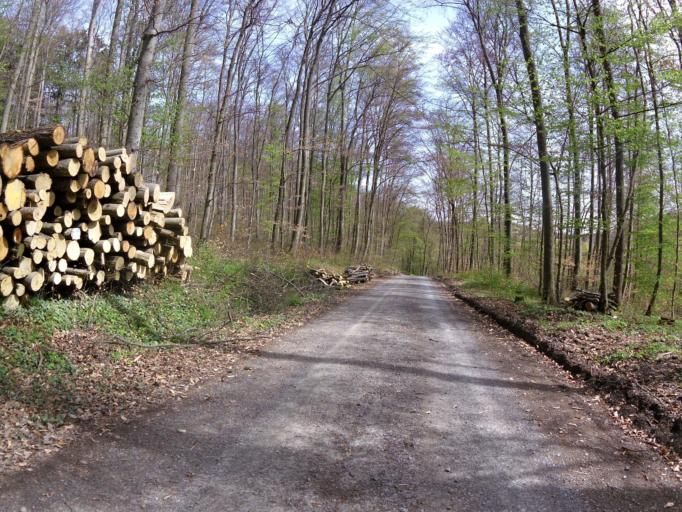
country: DE
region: Bavaria
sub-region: Regierungsbezirk Unterfranken
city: Rimpar
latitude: 49.8590
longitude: 9.9852
